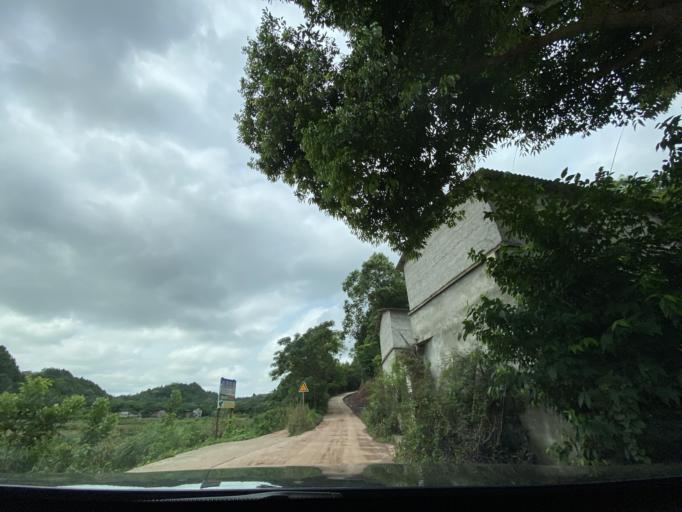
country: CN
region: Sichuan
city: Jiancheng
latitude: 30.4060
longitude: 104.5744
